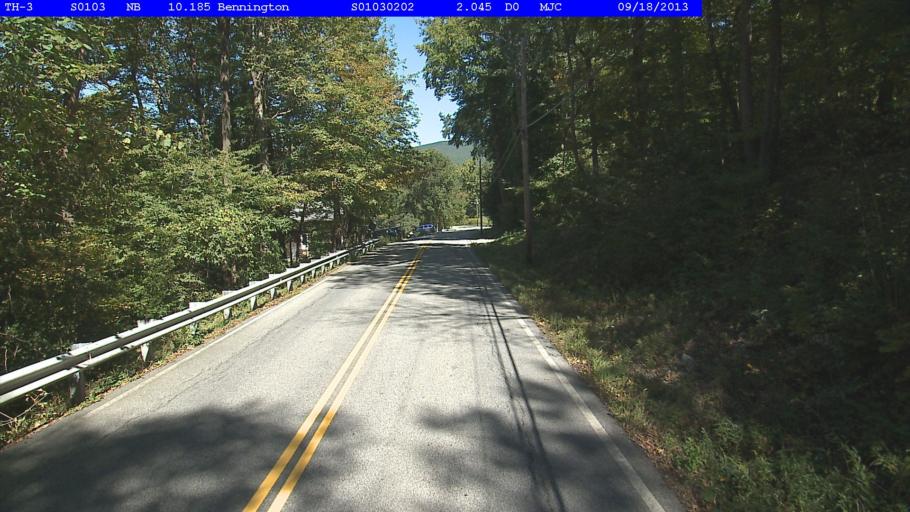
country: US
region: Vermont
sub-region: Bennington County
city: Bennington
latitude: 42.8655
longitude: -73.1753
